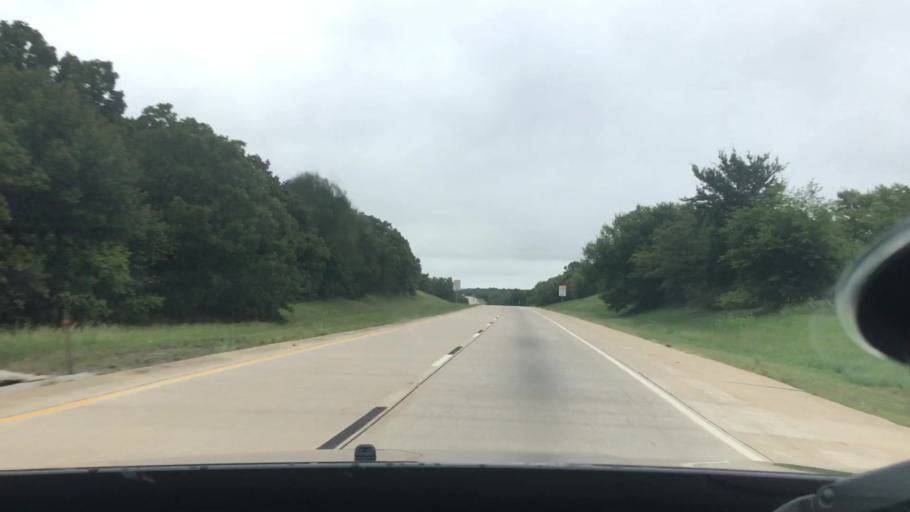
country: US
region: Oklahoma
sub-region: Okfuskee County
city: Okemah
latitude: 35.4283
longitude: -96.1764
